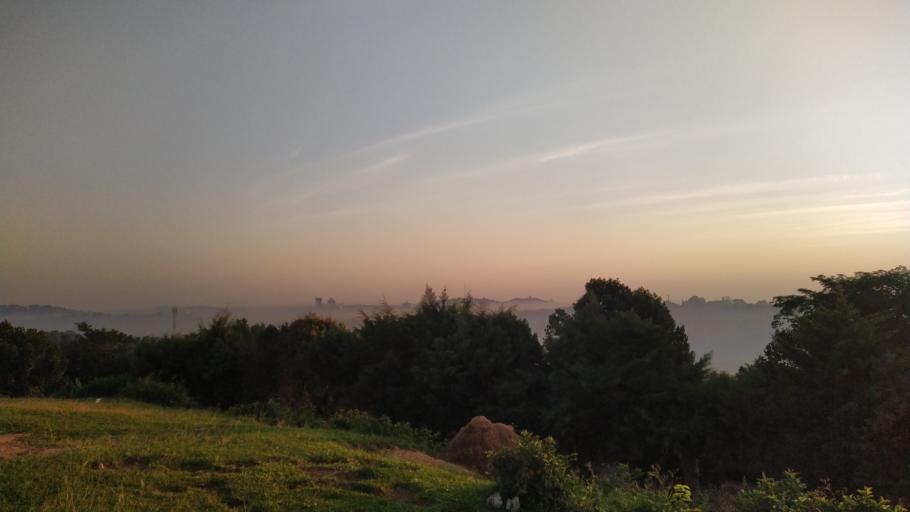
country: UG
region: Central Region
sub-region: Kampala District
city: Kampala
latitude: 0.2697
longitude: 32.5729
